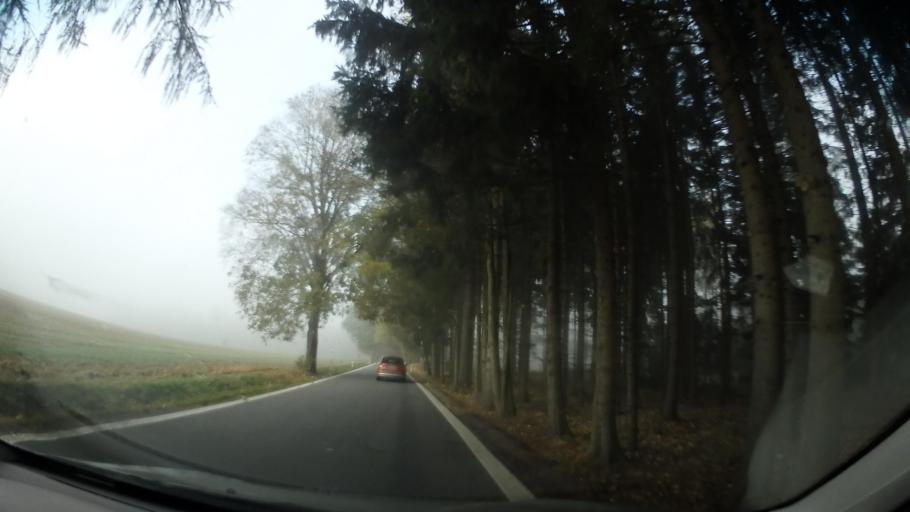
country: CZ
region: Vysocina
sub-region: Okres Zd'ar nad Sazavou
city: Nove Mesto na Morave
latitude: 49.4779
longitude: 16.0436
